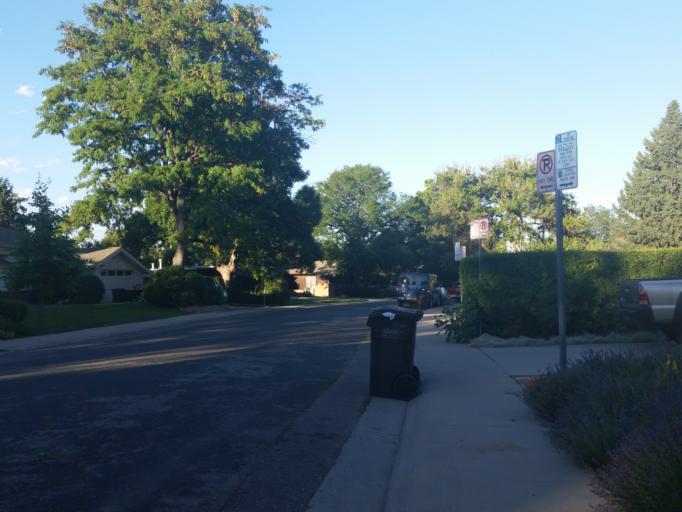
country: US
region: Colorado
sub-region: Boulder County
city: Boulder
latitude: 40.0095
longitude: -105.2629
